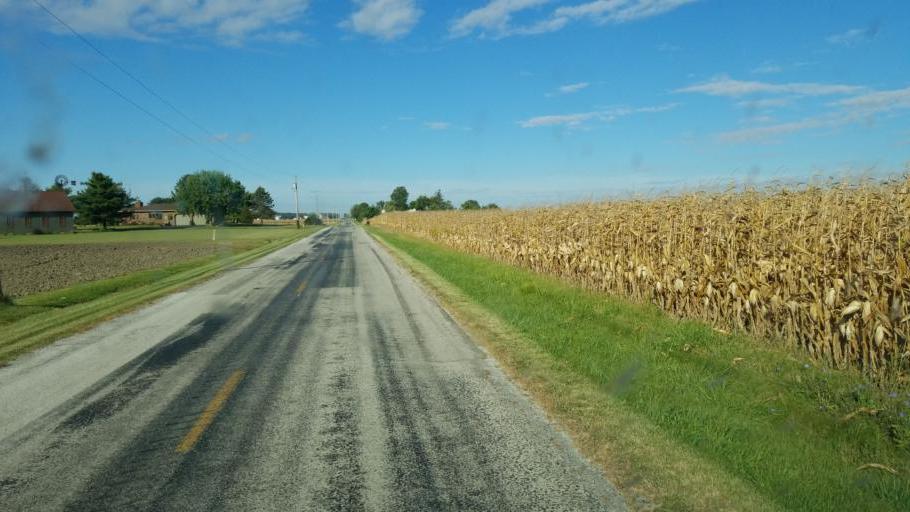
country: US
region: Ohio
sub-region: Marion County
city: Marion
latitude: 40.6886
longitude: -83.0547
